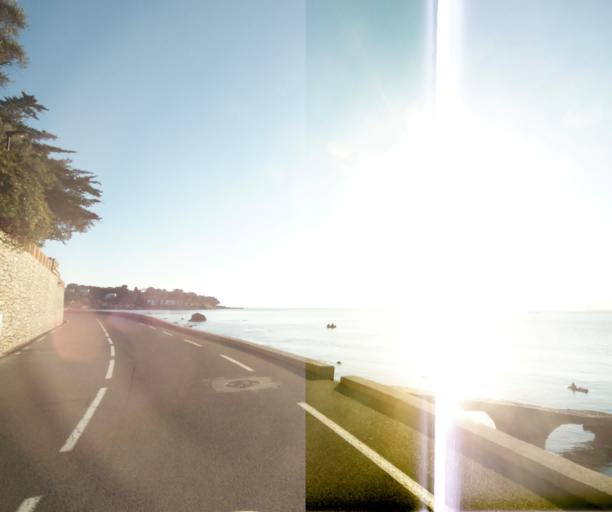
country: FR
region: Provence-Alpes-Cote d'Azur
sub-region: Departement des Alpes-Maritimes
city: Antibes
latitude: 43.5560
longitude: 7.1213
